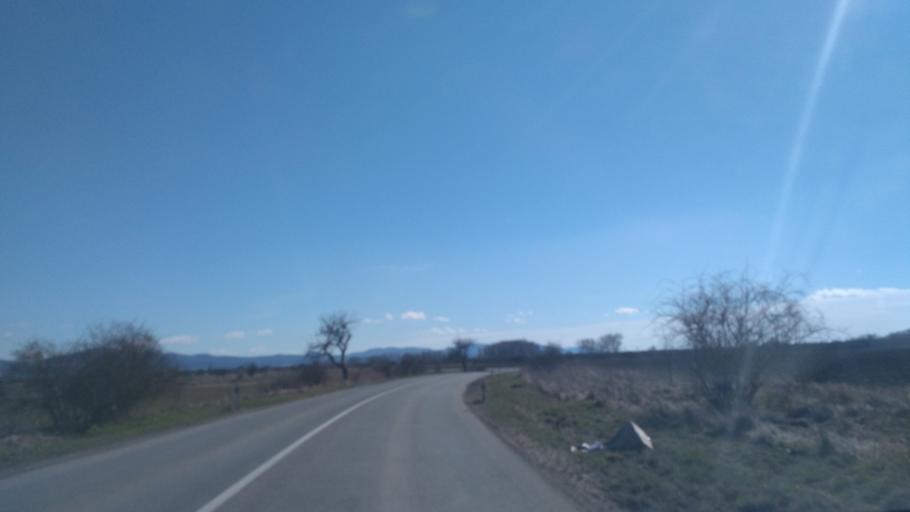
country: SK
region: Kosicky
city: Kosice
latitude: 48.6552
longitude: 21.2811
